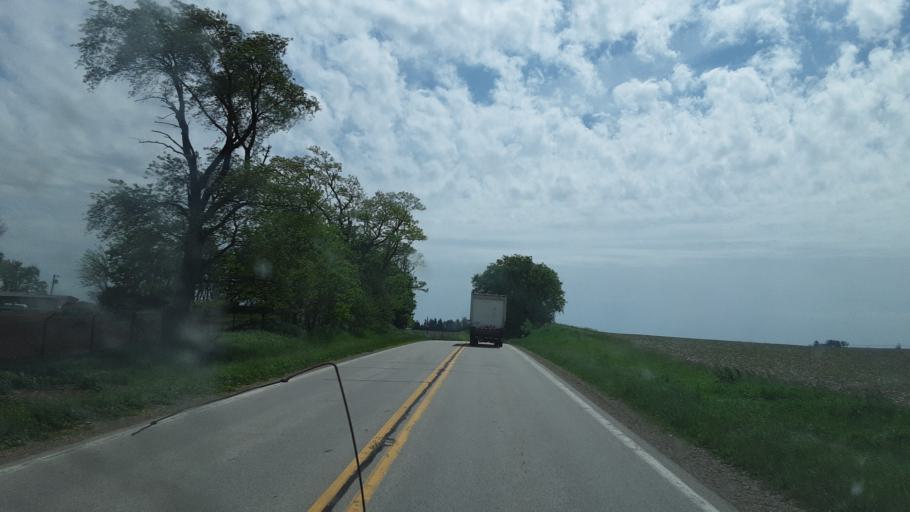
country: US
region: Illinois
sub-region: Logan County
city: Atlanta
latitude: 40.3107
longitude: -89.2611
